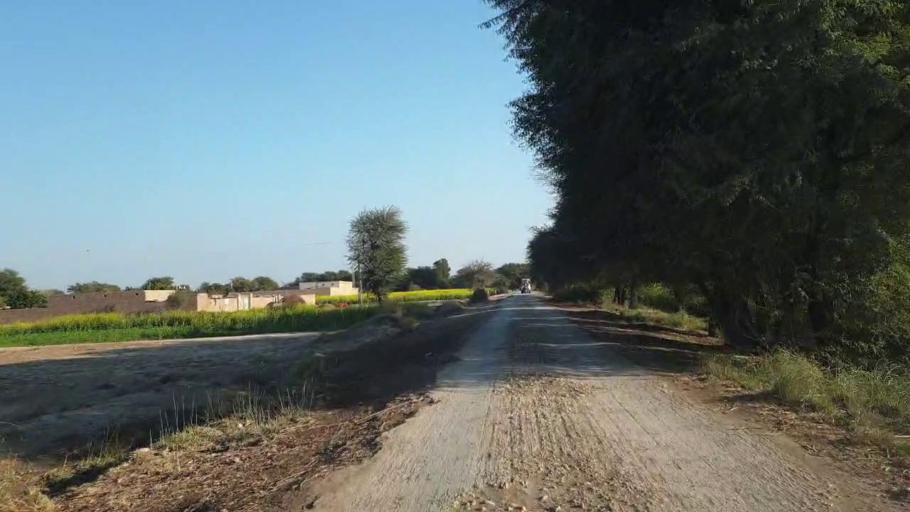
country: PK
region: Sindh
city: Shahpur Chakar
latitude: 26.1265
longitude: 68.5582
